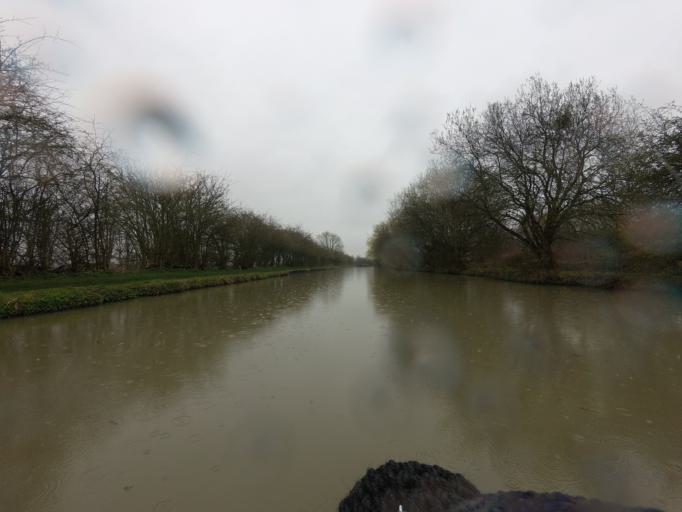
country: GB
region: England
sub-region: Northamptonshire
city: Blisworth
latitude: 52.1856
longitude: -0.9464
